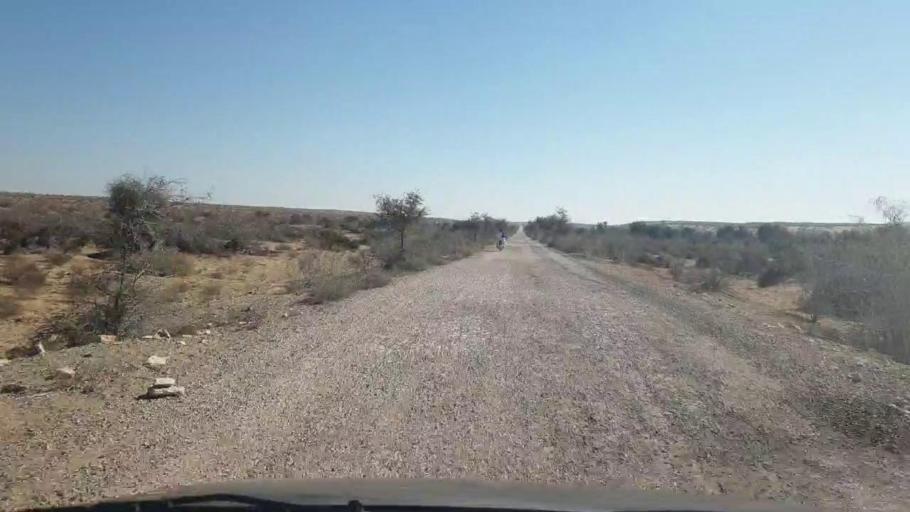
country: PK
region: Sindh
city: Bozdar
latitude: 27.0338
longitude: 68.6995
